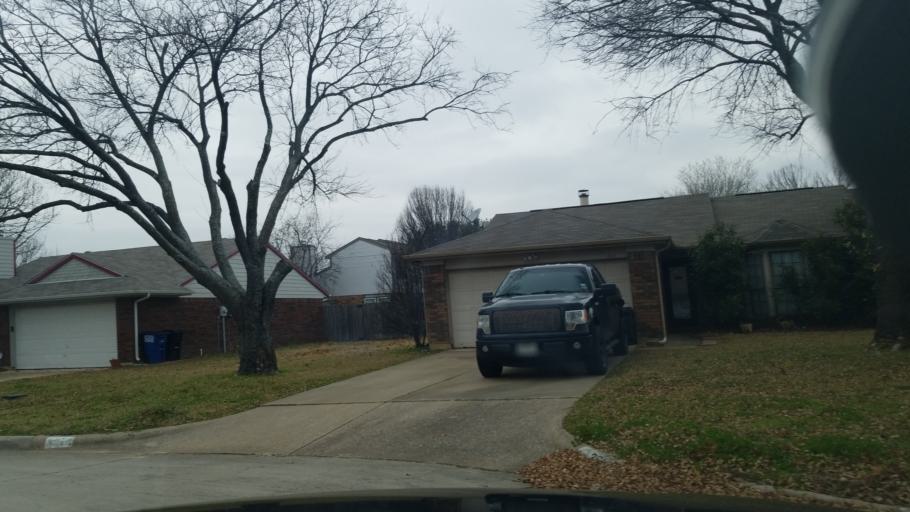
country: US
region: Texas
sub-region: Denton County
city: Hickory Creek
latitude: 33.1362
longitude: -97.0479
